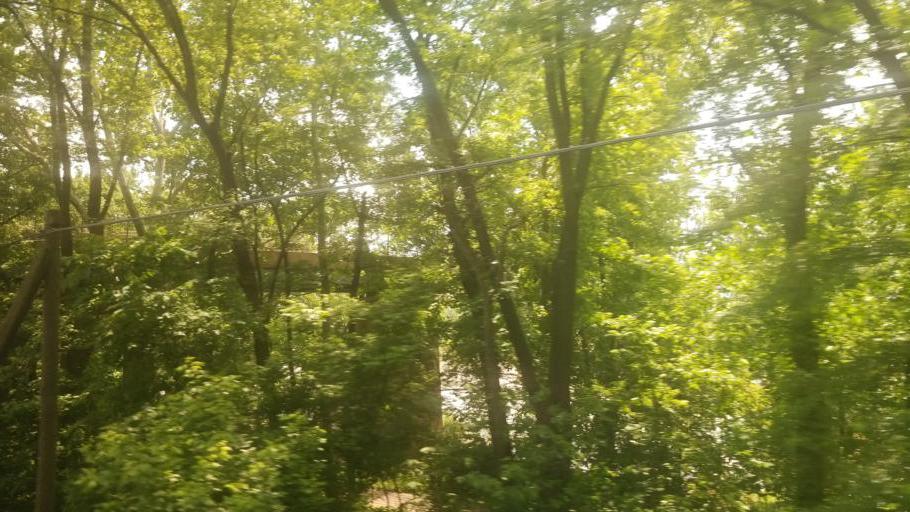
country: US
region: Maryland
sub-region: Frederick County
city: Point of Rocks
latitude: 39.2743
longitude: -77.5435
